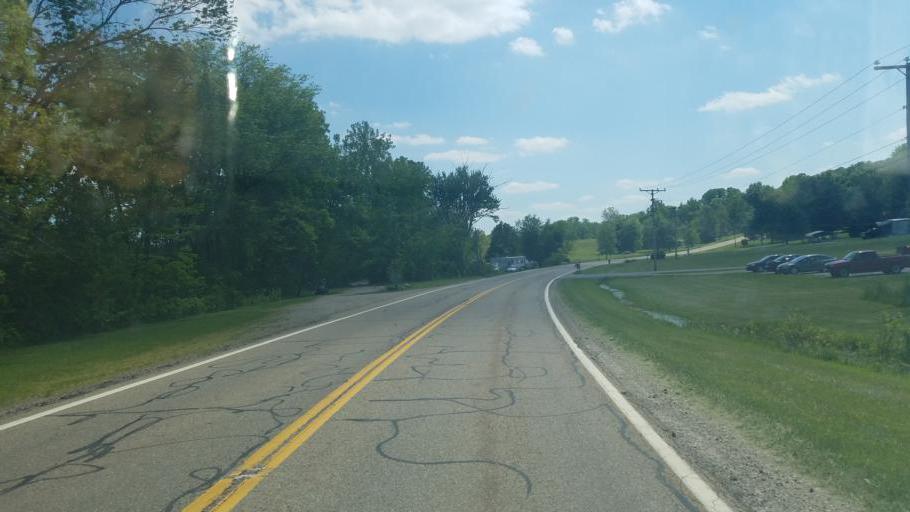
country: US
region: Ohio
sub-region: Muskingum County
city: Frazeysburg
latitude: 40.0798
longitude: -82.1577
